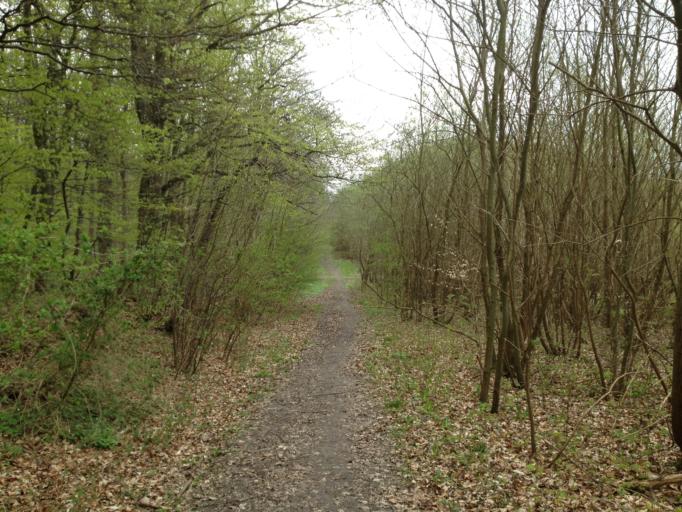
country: DK
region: Capital Region
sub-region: Fredensborg Kommune
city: Niva
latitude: 55.9454
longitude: 12.5128
